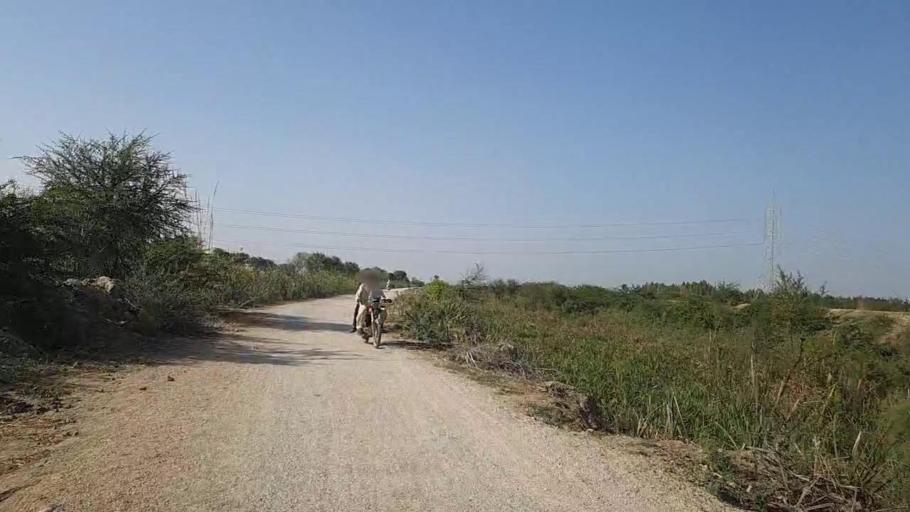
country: PK
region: Sindh
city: Kotri
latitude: 25.1503
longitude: 68.2650
